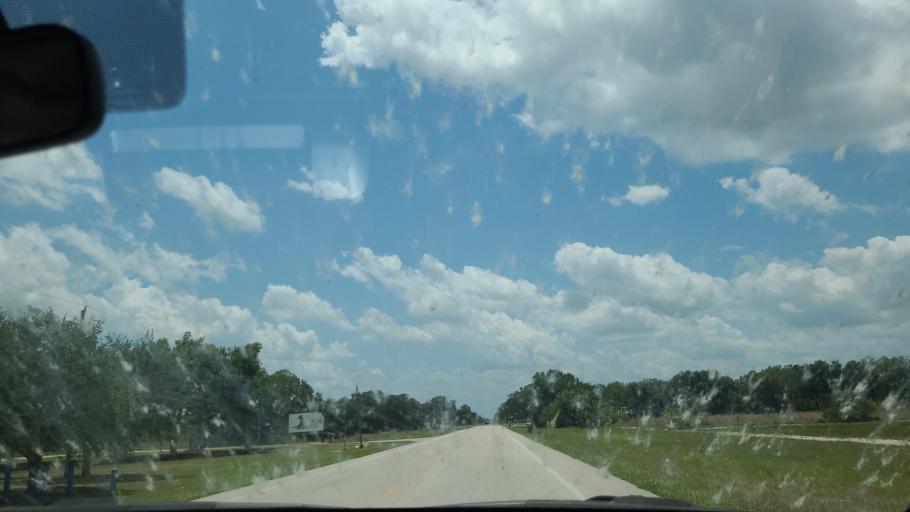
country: US
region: Florida
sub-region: Glades County
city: Buckhead Ridge
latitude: 27.0976
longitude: -81.0701
